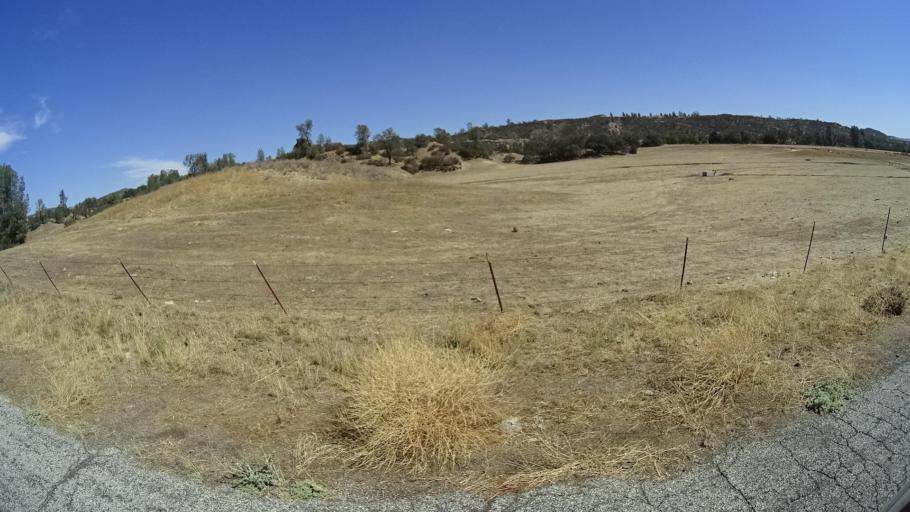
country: US
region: California
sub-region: San Luis Obispo County
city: San Miguel
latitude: 36.0242
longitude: -120.6546
